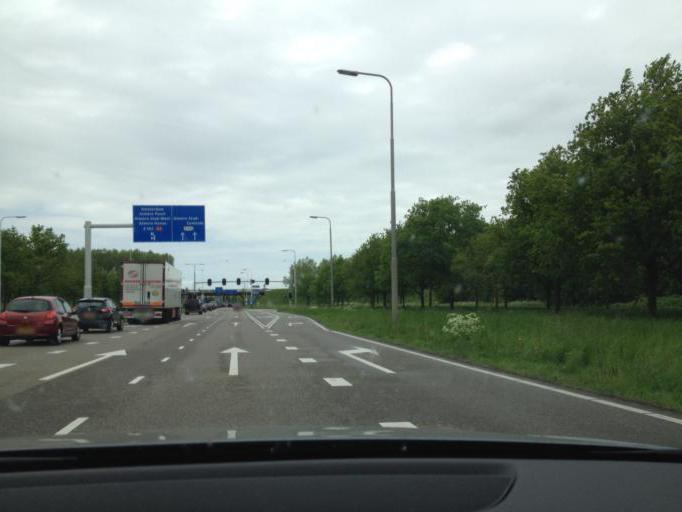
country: NL
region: Flevoland
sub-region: Gemeente Almere
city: Almere Stad
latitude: 52.3535
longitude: 5.2585
